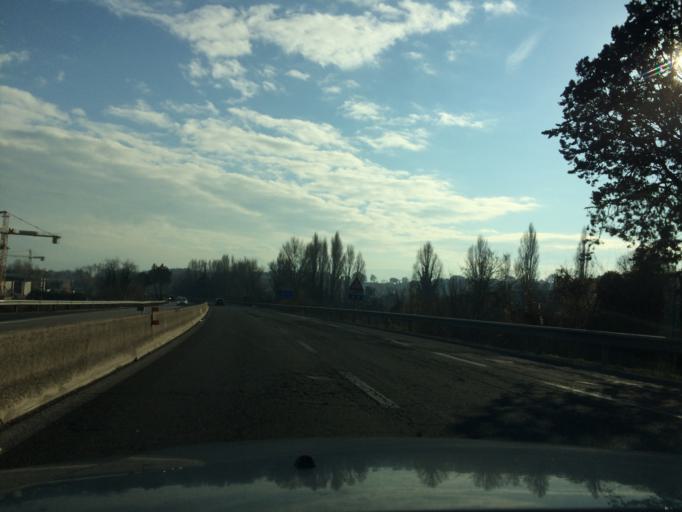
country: IT
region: Umbria
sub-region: Provincia di Terni
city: San Gemini
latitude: 42.5935
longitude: 12.5634
